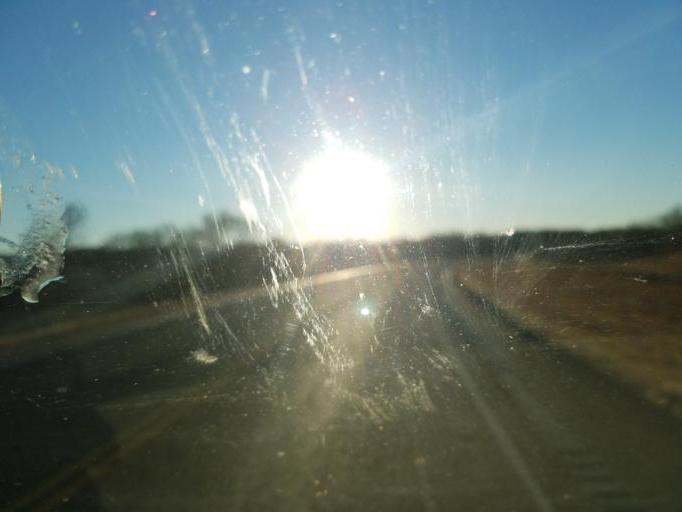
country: US
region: South Dakota
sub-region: Bon Homme County
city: Springfield
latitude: 42.8658
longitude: -97.8938
